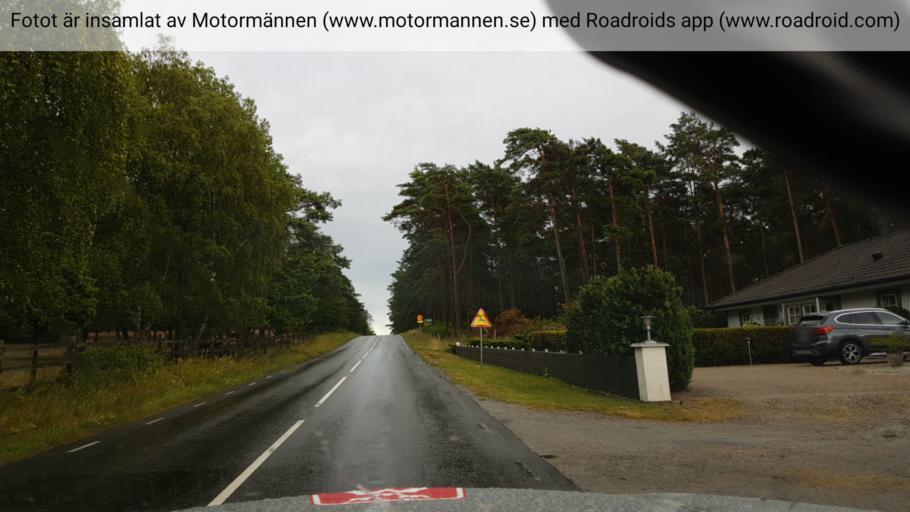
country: SE
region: Blekinge
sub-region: Solvesborgs Kommun
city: Soelvesborg
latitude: 56.0162
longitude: 14.6835
